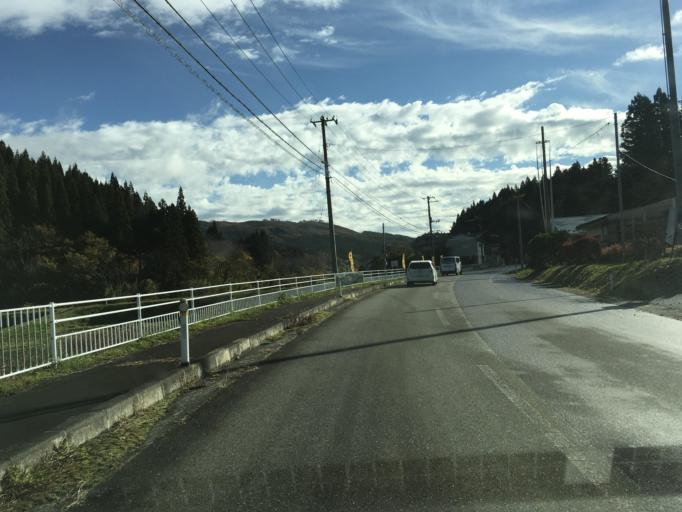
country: JP
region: Iwate
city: Ichinoseki
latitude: 38.8947
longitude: 141.4384
